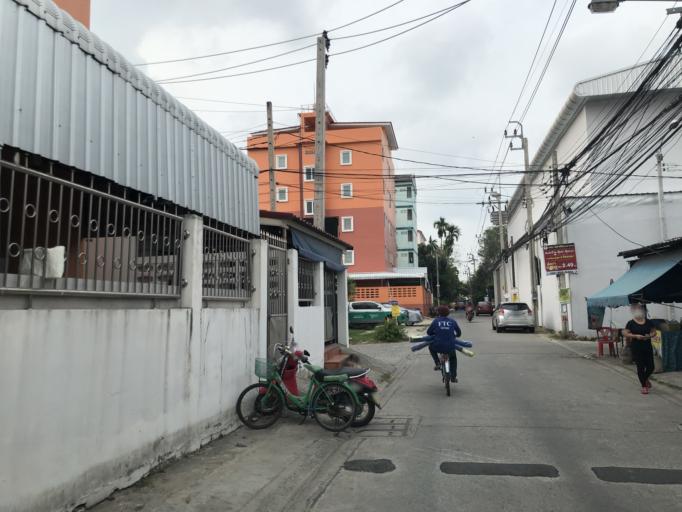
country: TH
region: Bangkok
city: Bang Na
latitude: 13.6052
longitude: 100.6819
